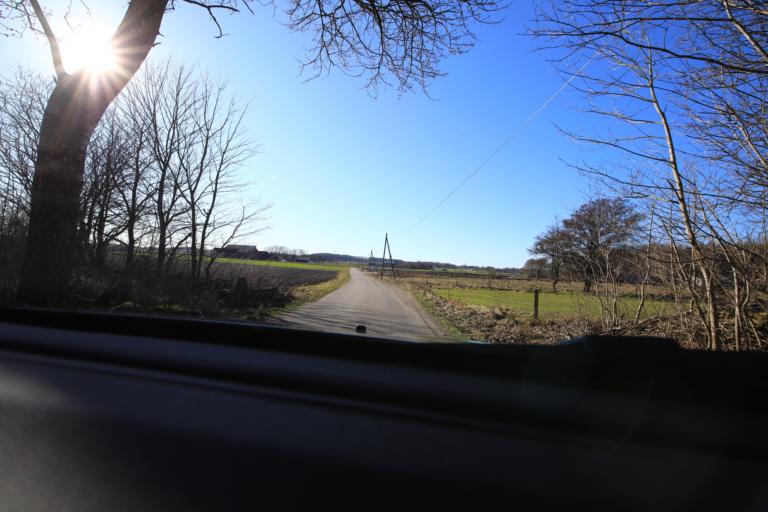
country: SE
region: Halland
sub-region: Varbergs Kommun
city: Tvaaker
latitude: 57.0634
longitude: 12.4210
